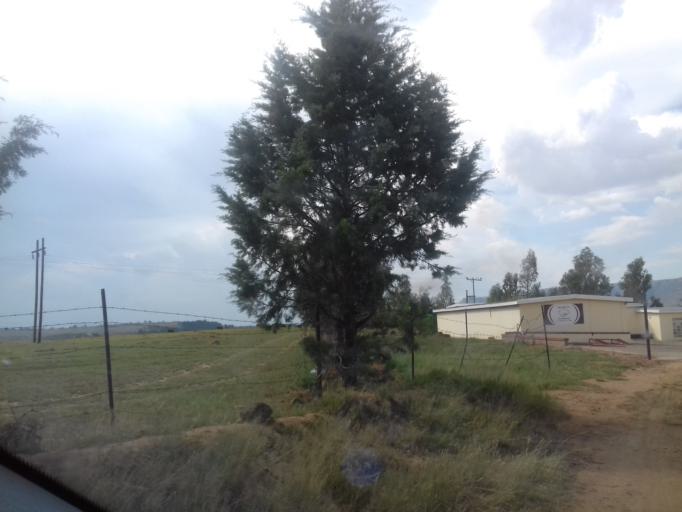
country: LS
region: Mafeteng
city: Mafeteng
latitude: -29.6888
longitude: 27.4341
